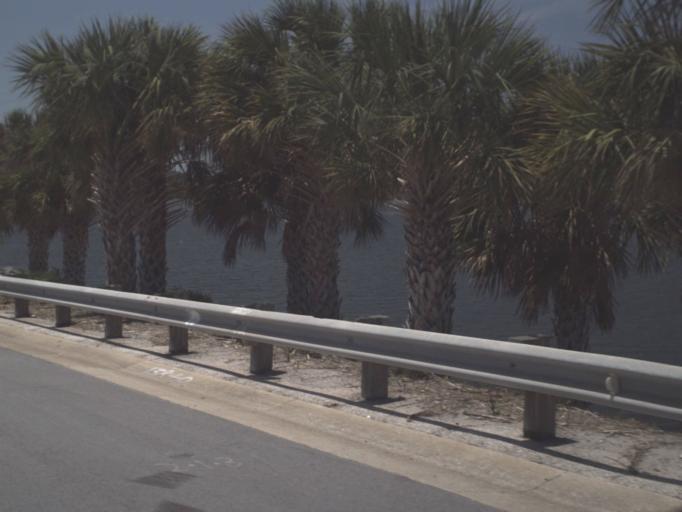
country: US
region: Florida
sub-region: Brevard County
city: Melbourne
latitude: 28.0827
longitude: -80.5959
